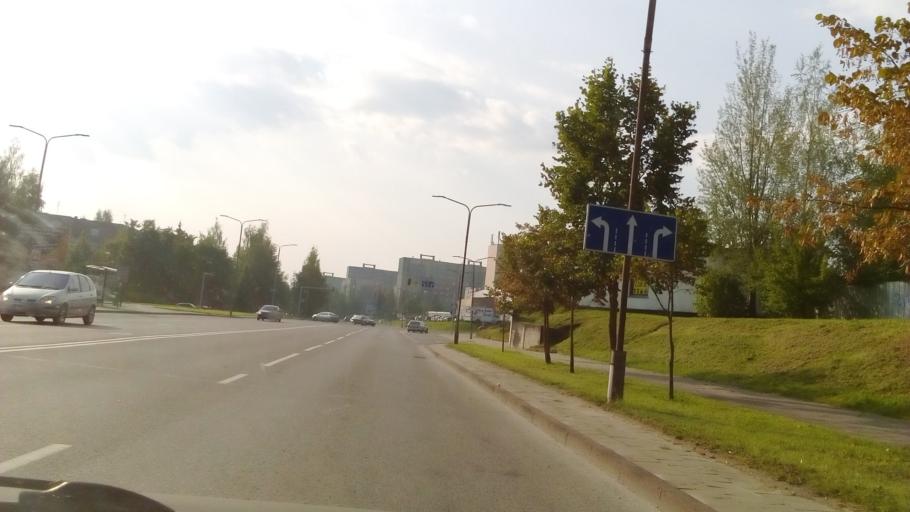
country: LT
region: Alytaus apskritis
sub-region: Alytus
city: Alytus
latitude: 54.3951
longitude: 24.0173
